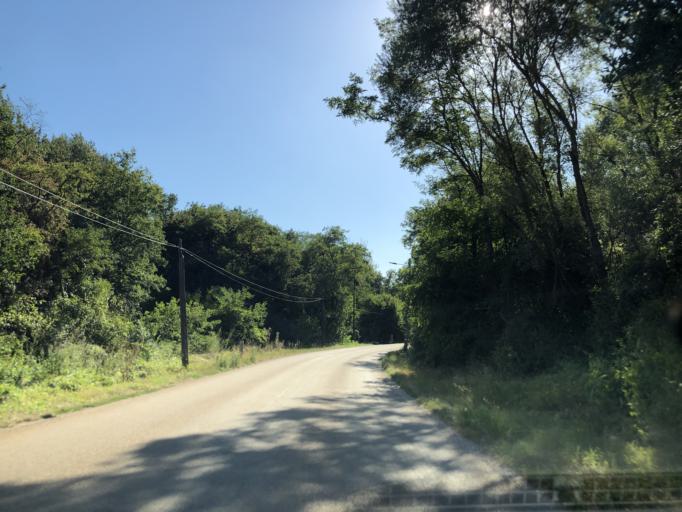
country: FR
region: Bourgogne
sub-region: Departement de l'Yonne
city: Cheny
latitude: 47.9265
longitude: 3.5402
